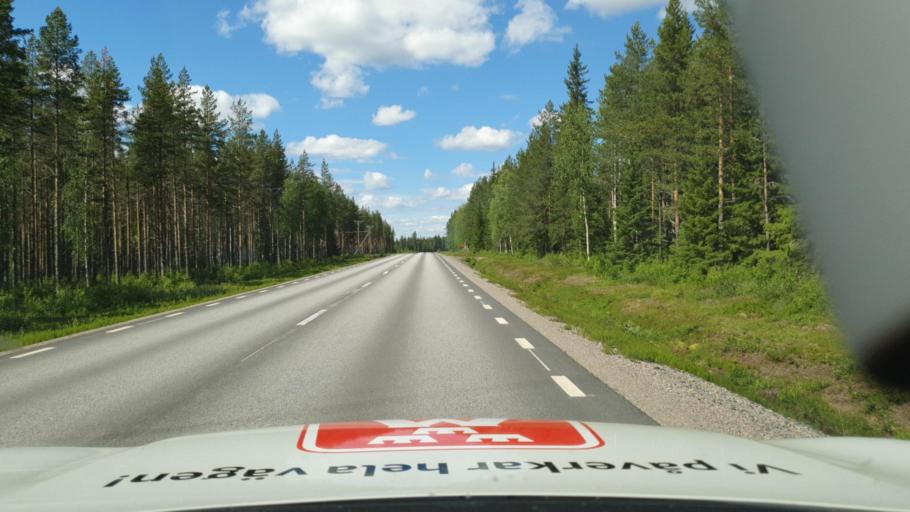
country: SE
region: Vaesterbotten
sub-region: Skelleftea Kommun
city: Boliden
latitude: 64.9322
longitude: 20.3050
